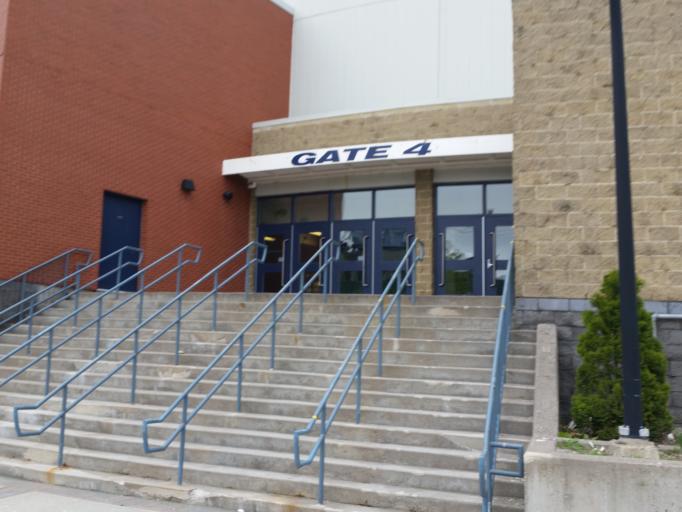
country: CA
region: Newfoundland and Labrador
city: St. John's
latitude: 47.5608
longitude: -52.7126
